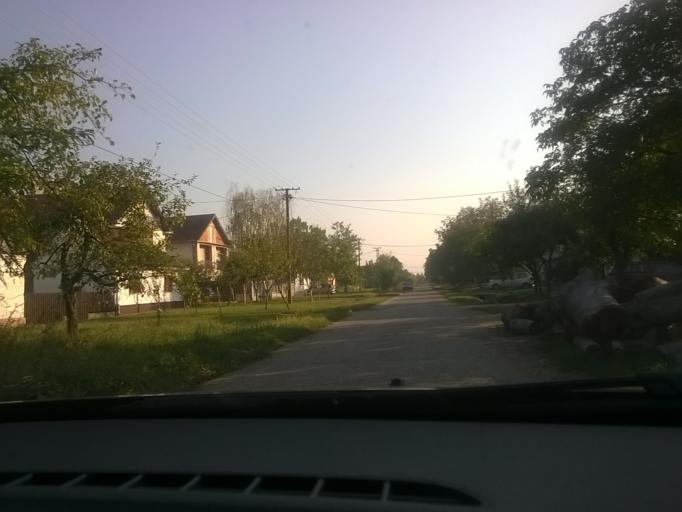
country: RS
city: Pavlis
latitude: 45.1047
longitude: 21.2425
